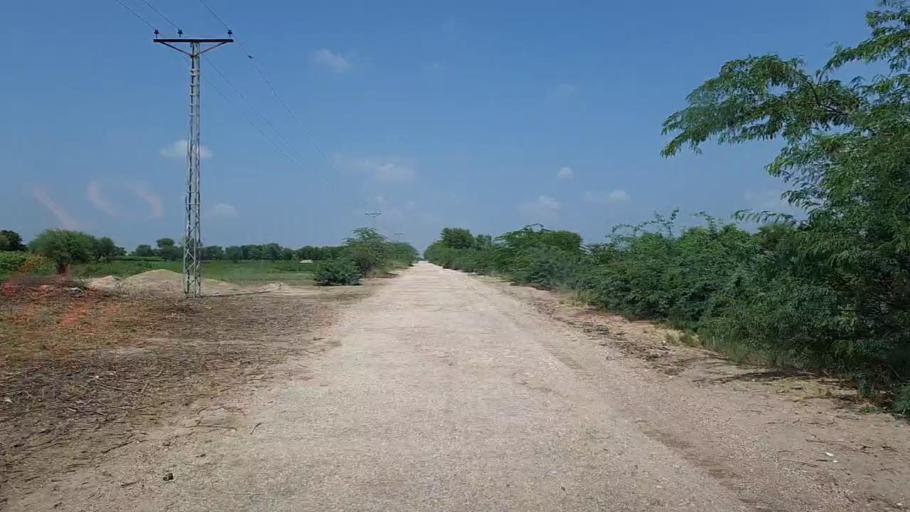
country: PK
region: Sindh
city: Kandiaro
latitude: 26.9893
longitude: 68.2474
